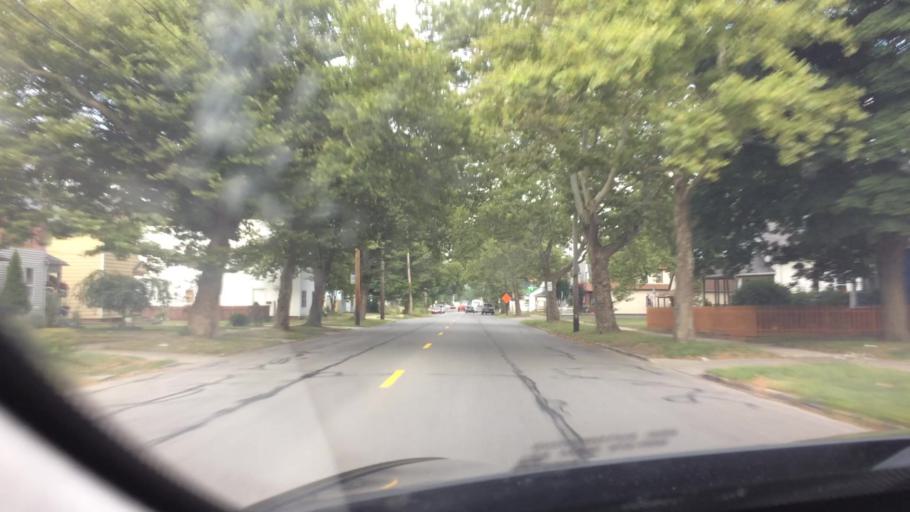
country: US
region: Ohio
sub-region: Wood County
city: Rossford
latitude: 41.6308
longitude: -83.5709
